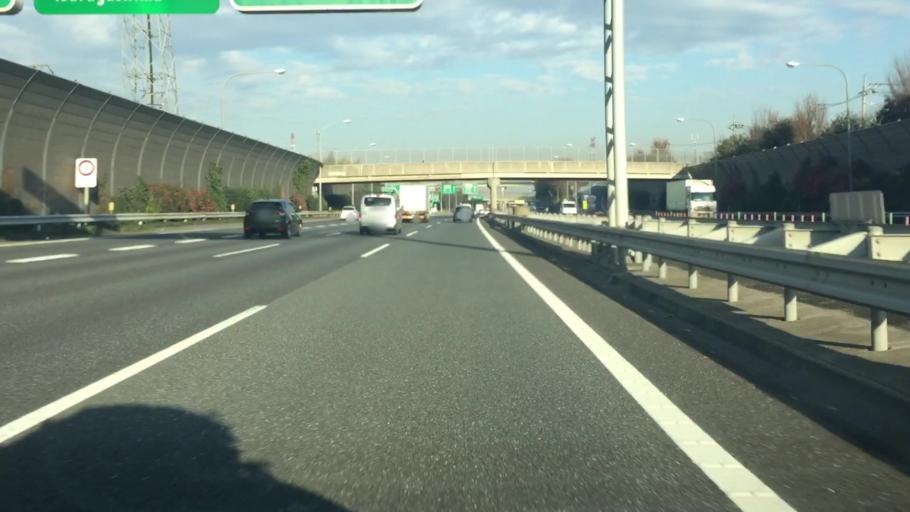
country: JP
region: Saitama
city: Sakado
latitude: 35.9281
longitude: 139.4094
